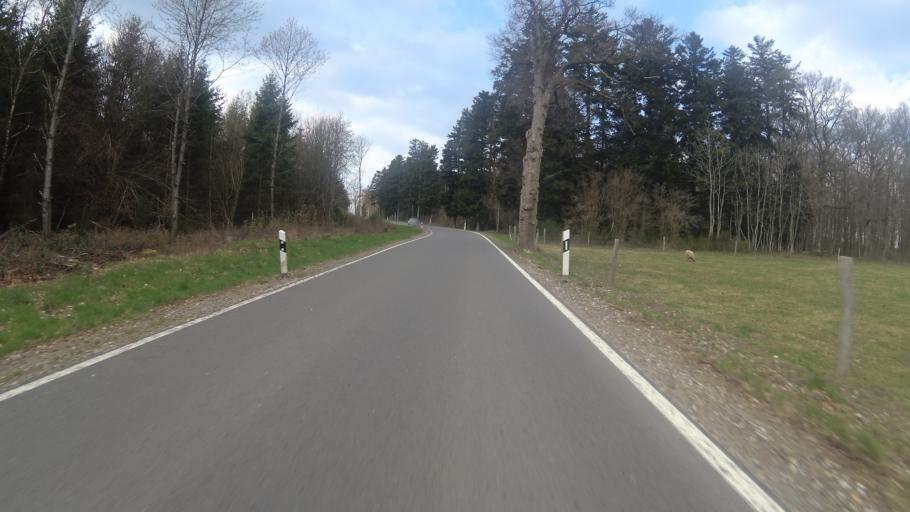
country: DE
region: Rheinland-Pfalz
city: Bescheid
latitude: 49.7555
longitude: 6.8659
